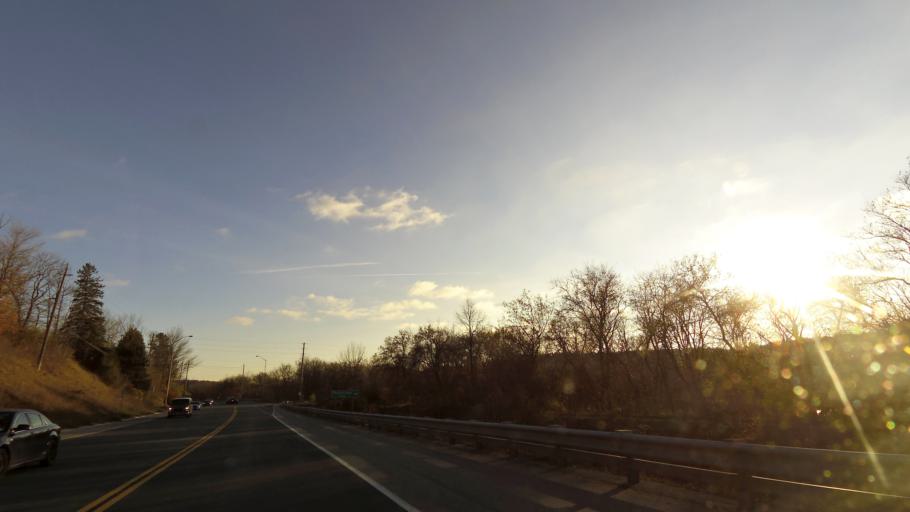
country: CA
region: Ontario
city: Cambridge
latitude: 43.3191
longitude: -80.3130
